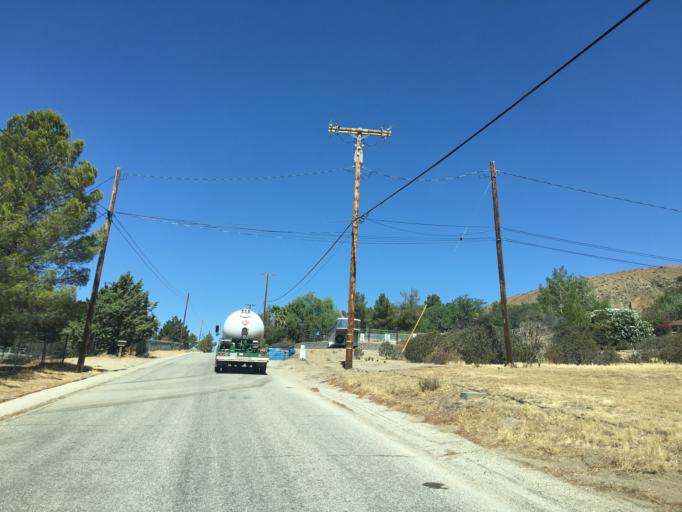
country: US
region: California
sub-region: Los Angeles County
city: Leona Valley
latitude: 34.6228
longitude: -118.2891
